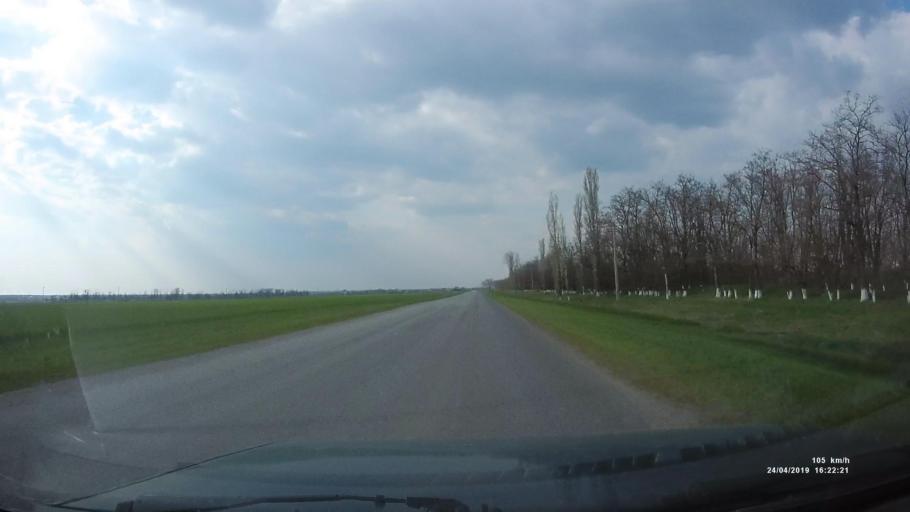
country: RU
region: Rostov
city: Orlovskiy
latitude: 46.8183
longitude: 42.0568
